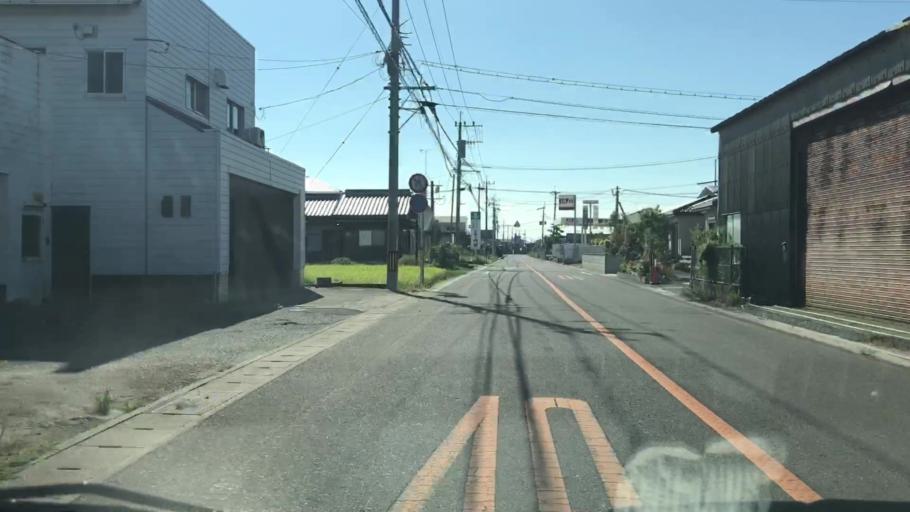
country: JP
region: Saga Prefecture
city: Okawa
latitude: 33.1893
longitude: 130.3246
